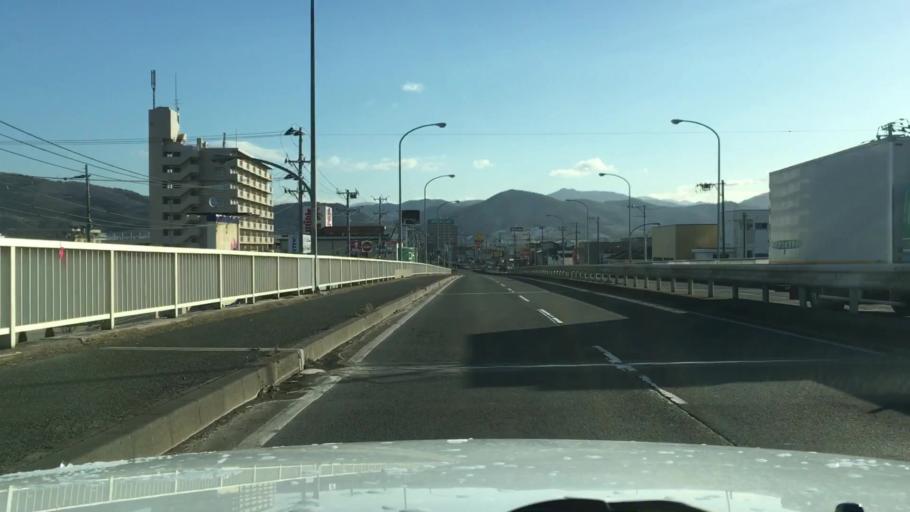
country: JP
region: Iwate
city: Morioka-shi
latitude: 39.6570
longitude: 141.1481
